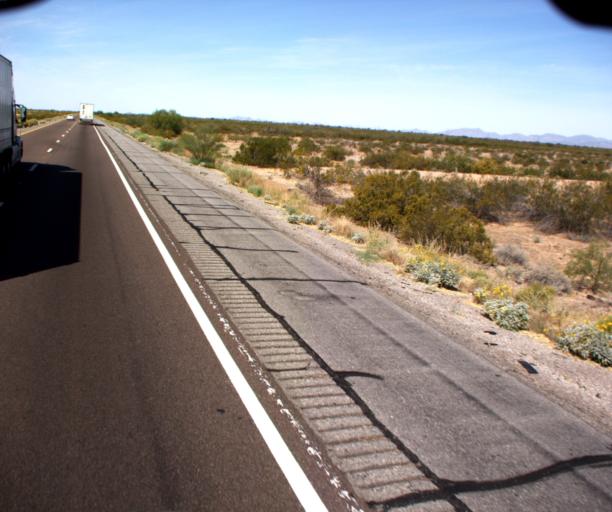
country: US
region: Arizona
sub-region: La Paz County
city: Salome
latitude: 33.5469
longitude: -113.2059
